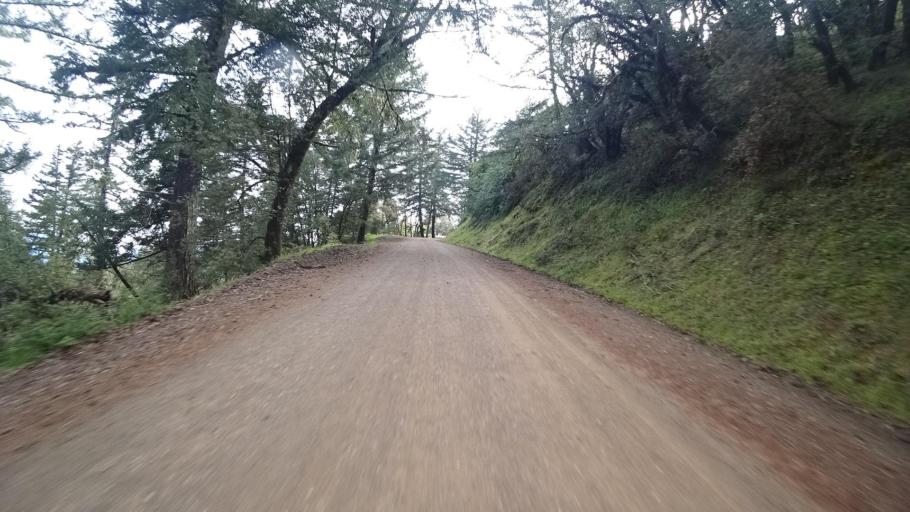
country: US
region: California
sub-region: Humboldt County
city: Redway
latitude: 40.2048
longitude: -123.7192
